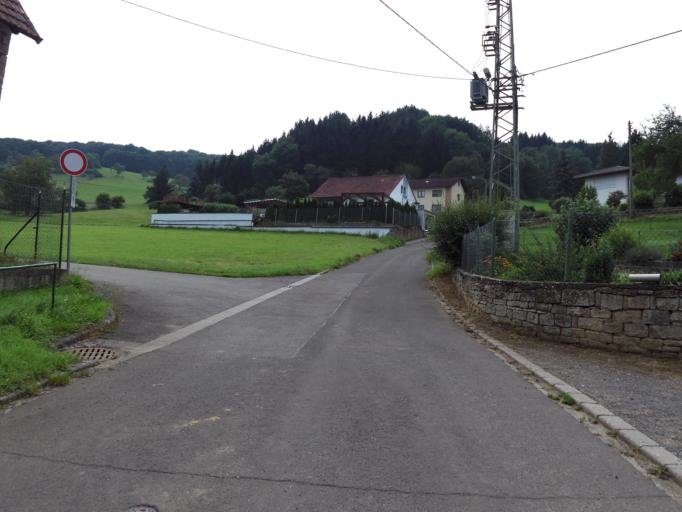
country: DE
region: Rheinland-Pfalz
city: Bayerfeld-Steckweiler
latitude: 49.6740
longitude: 7.8019
